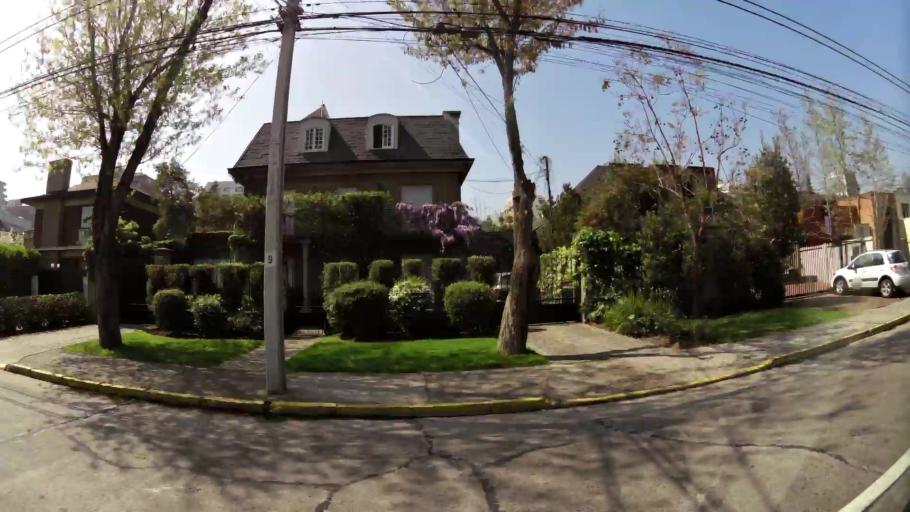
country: CL
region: Santiago Metropolitan
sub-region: Provincia de Santiago
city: Villa Presidente Frei, Nunoa, Santiago, Chile
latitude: -33.4010
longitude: -70.5892
